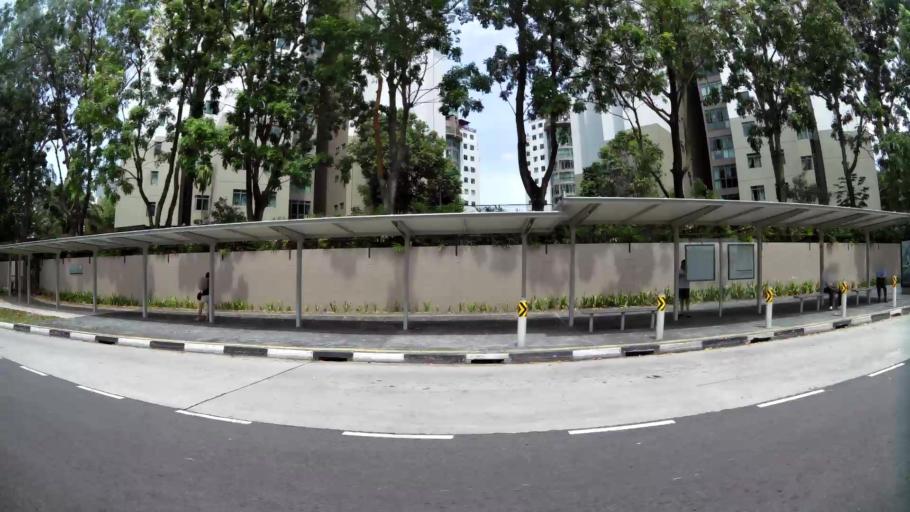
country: MY
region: Johor
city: Johor Bahru
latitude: 1.3416
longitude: 103.7123
